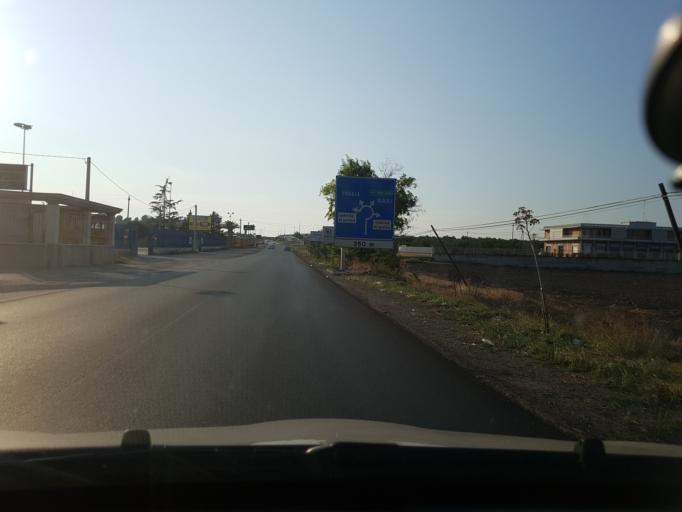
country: IT
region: Apulia
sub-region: Provincia di Foggia
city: Cerignola
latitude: 41.2712
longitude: 15.8792
